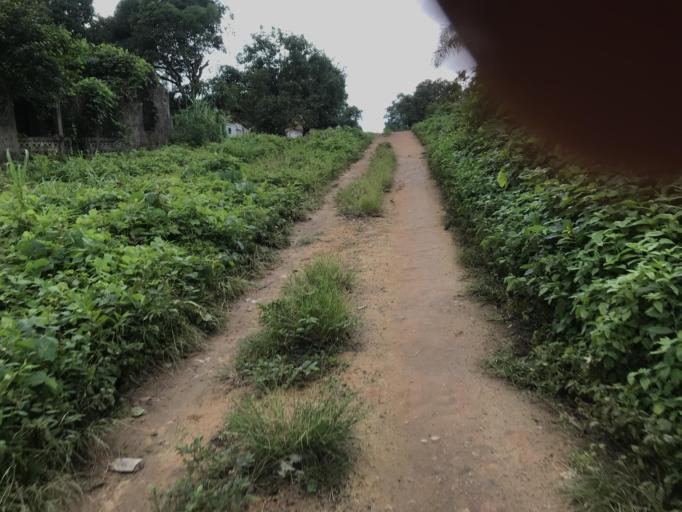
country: GN
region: Nzerekore
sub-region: Prefecture de Guekedou
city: Gueckedou
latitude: 8.4726
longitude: -10.2834
